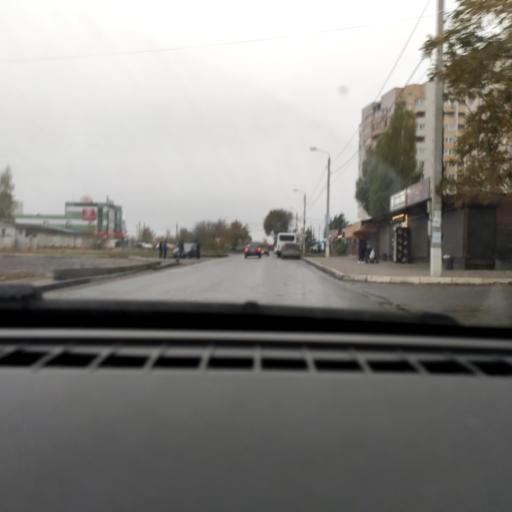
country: RU
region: Voronezj
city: Somovo
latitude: 51.6708
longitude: 39.2918
